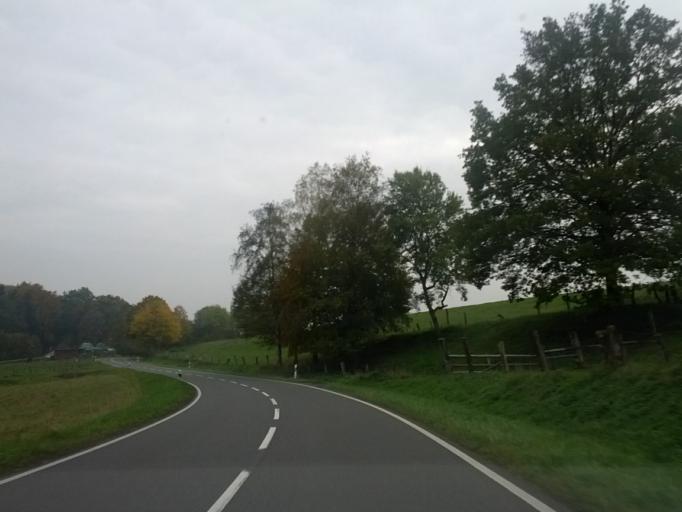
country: DE
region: Hesse
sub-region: Regierungsbezirk Kassel
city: Herleshausen
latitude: 51.0239
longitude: 10.1493
